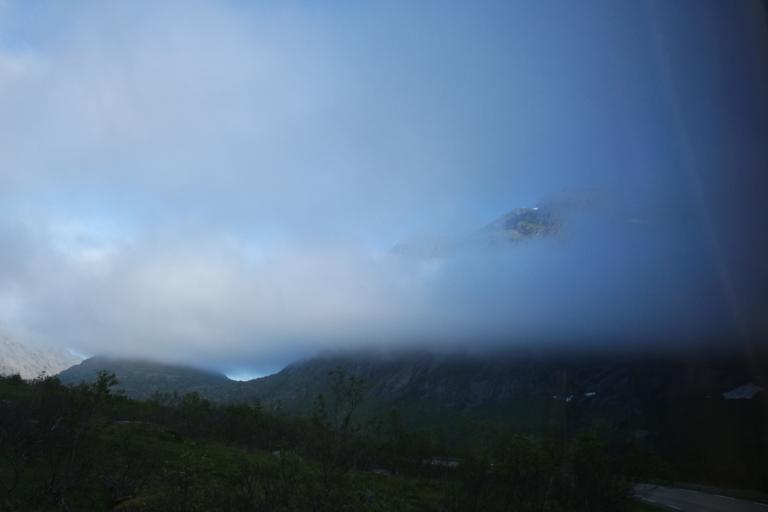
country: NO
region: Nordland
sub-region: Flakstad
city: Ramberg
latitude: 68.0605
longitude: 13.3166
